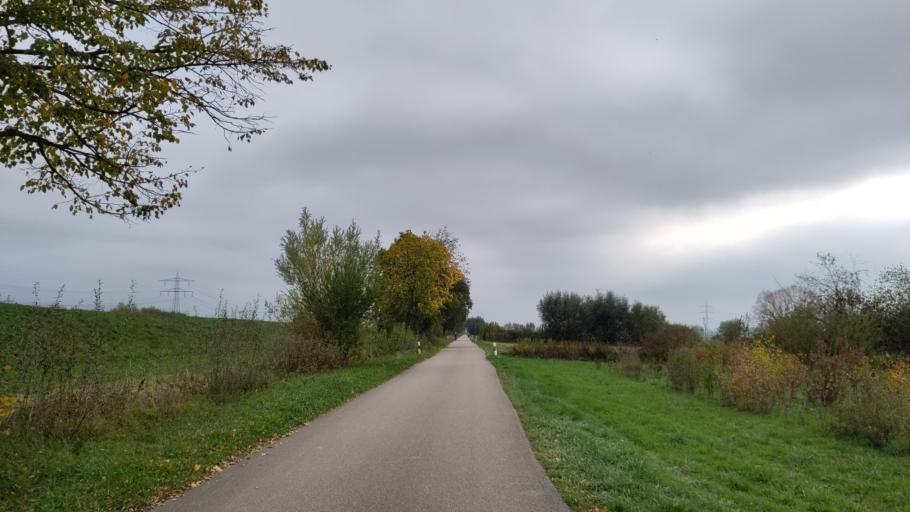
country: DE
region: Baden-Wuerttemberg
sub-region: Freiburg Region
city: Riegel
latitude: 48.1433
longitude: 7.7552
